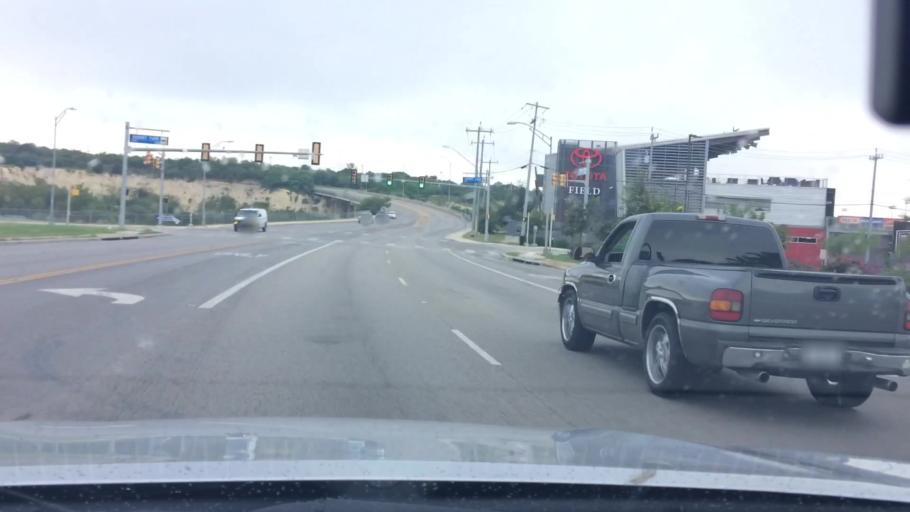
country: US
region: Texas
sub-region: Bexar County
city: Windcrest
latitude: 29.5380
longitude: -98.3953
